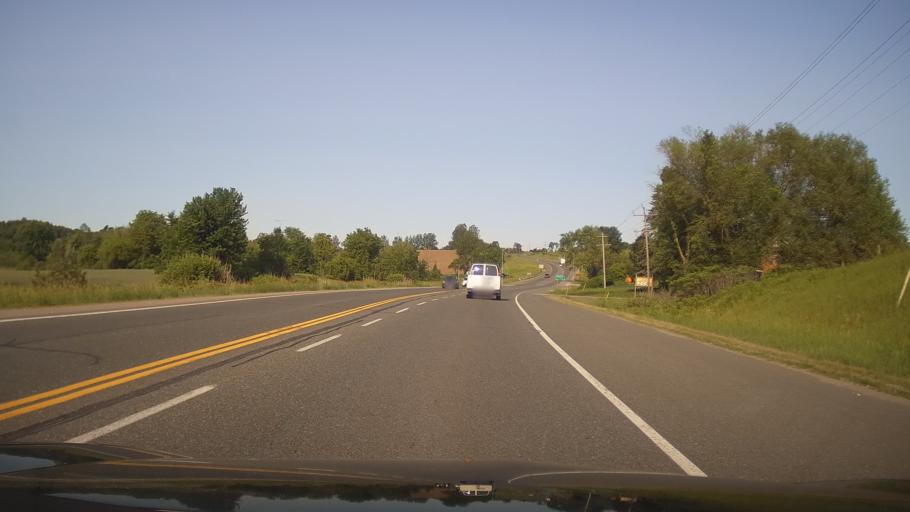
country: CA
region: Ontario
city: Peterborough
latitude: 44.3652
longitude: -78.0030
